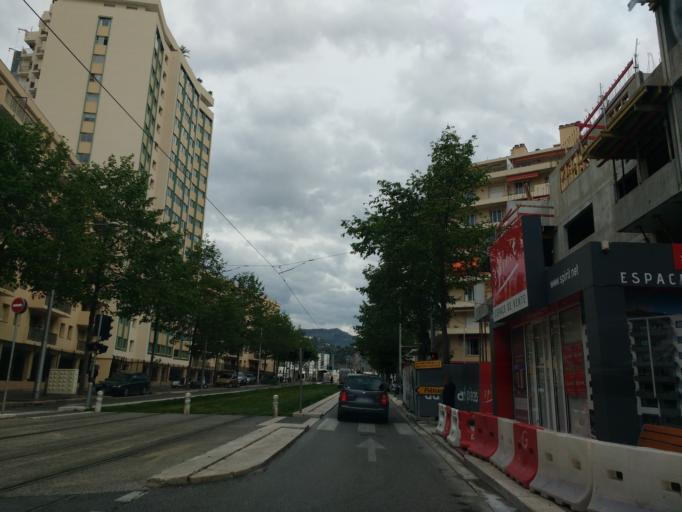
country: FR
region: Provence-Alpes-Cote d'Azur
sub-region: Departement des Alpes-Maritimes
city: Saint-Andre-de-la-Roche
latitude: 43.7173
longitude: 7.2922
